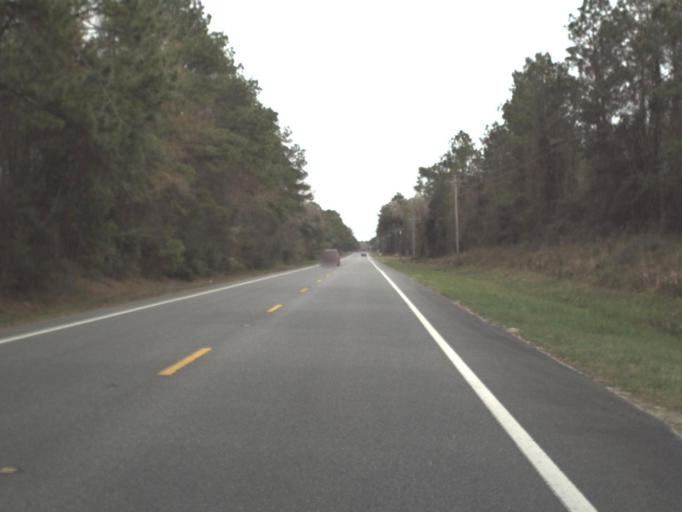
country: US
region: Florida
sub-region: Wakulla County
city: Crawfordville
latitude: 30.2569
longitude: -84.3474
